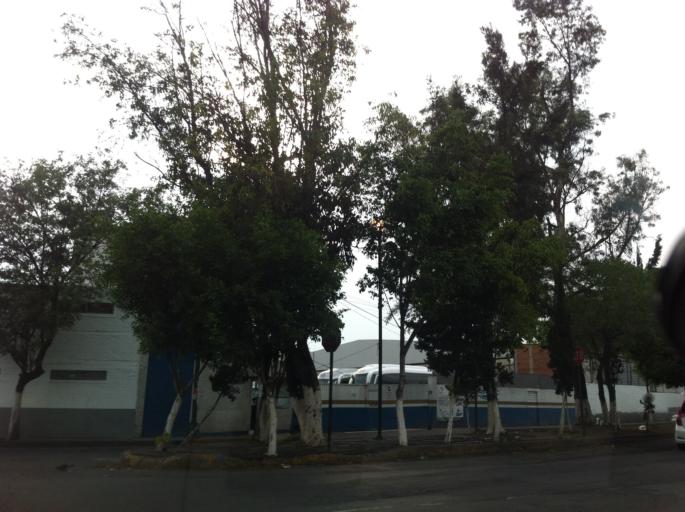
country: MX
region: Mexico
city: Colonia Lindavista
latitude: 19.4811
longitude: -99.1369
